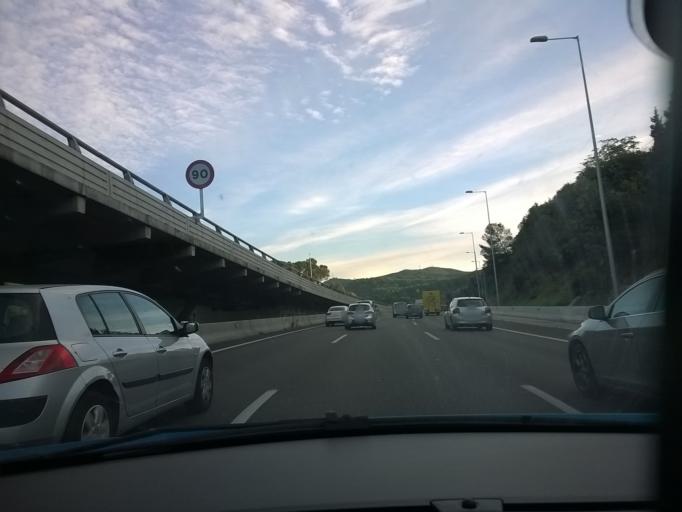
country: ES
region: Catalonia
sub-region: Provincia de Barcelona
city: Ripollet
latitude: 41.4766
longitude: 2.1628
